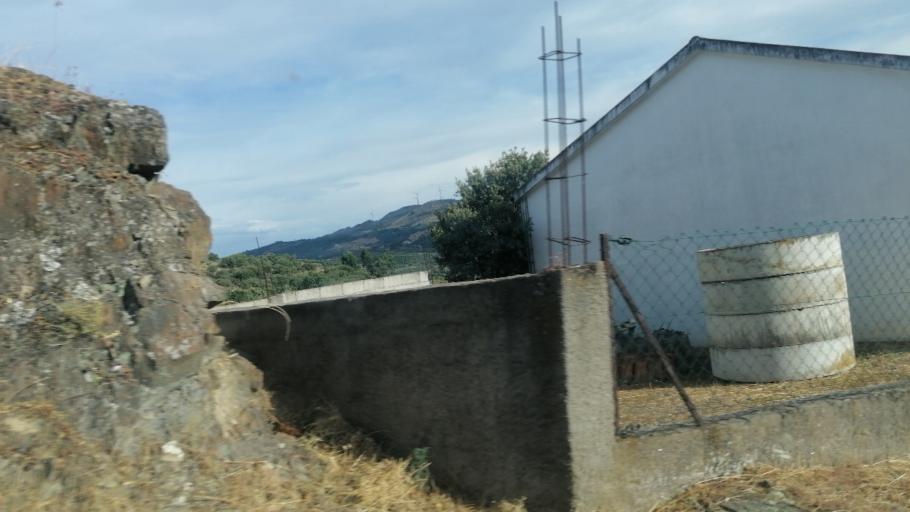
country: PT
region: Viseu
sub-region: Sao Joao da Pesqueira
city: Sao Joao da Pesqueira
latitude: 41.1023
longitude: -7.4588
